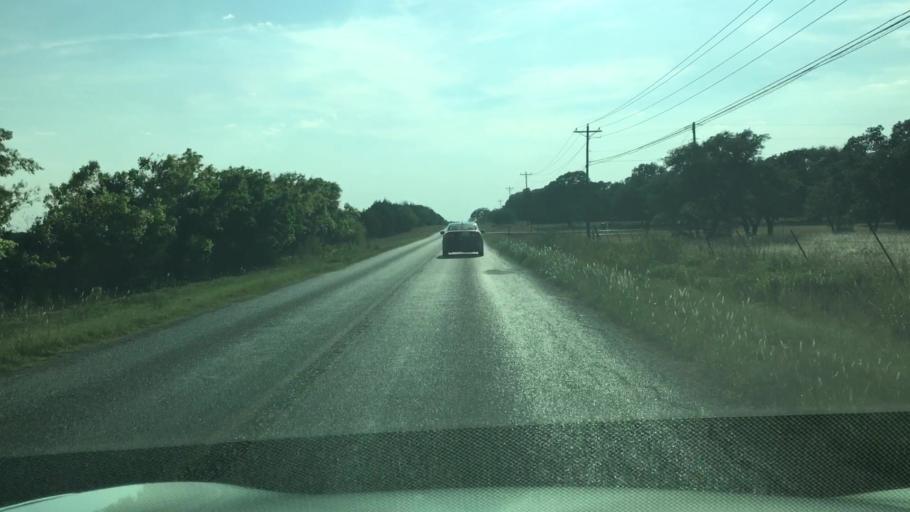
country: US
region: Texas
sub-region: Hays County
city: Dripping Springs
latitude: 30.1537
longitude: -98.0016
